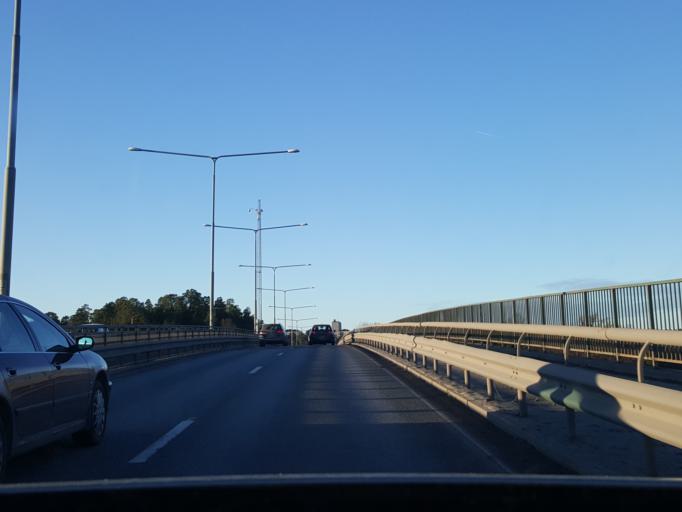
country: SE
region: Stockholm
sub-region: Lidingo
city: Brevik
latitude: 59.3143
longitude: 18.2234
